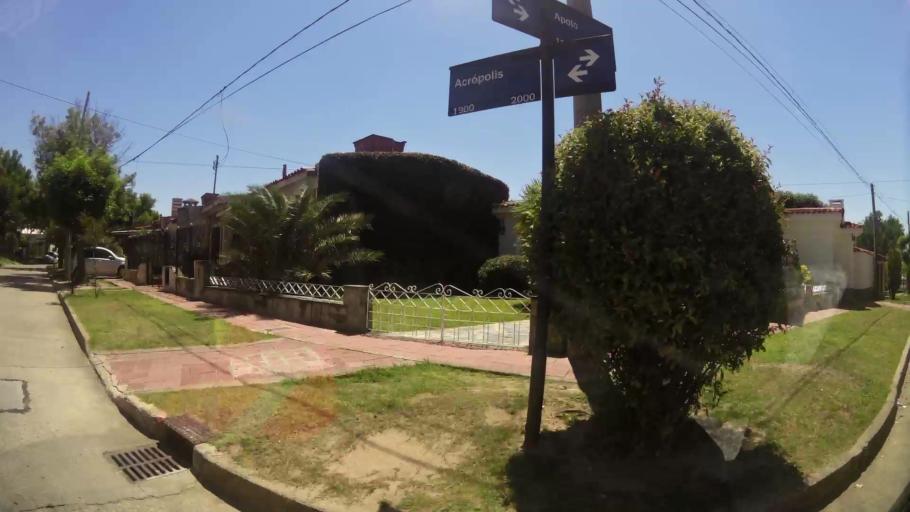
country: AR
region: Cordoba
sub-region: Departamento de Capital
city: Cordoba
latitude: -31.4346
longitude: -64.2107
